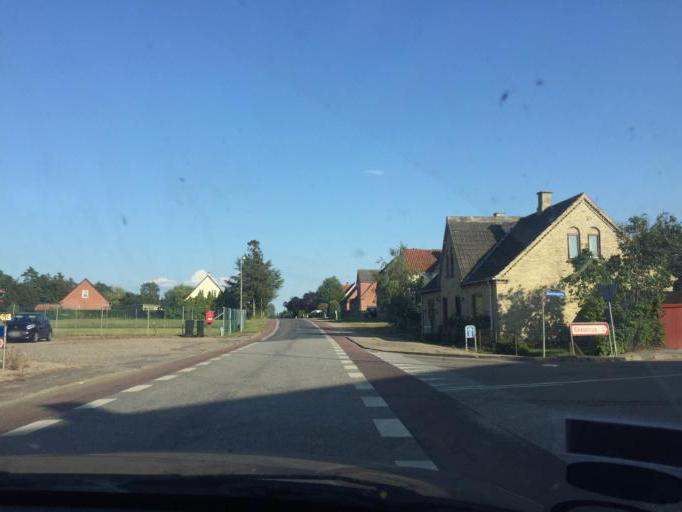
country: DK
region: Zealand
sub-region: Lolland Kommune
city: Maribo
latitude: 54.7979
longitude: 11.5219
